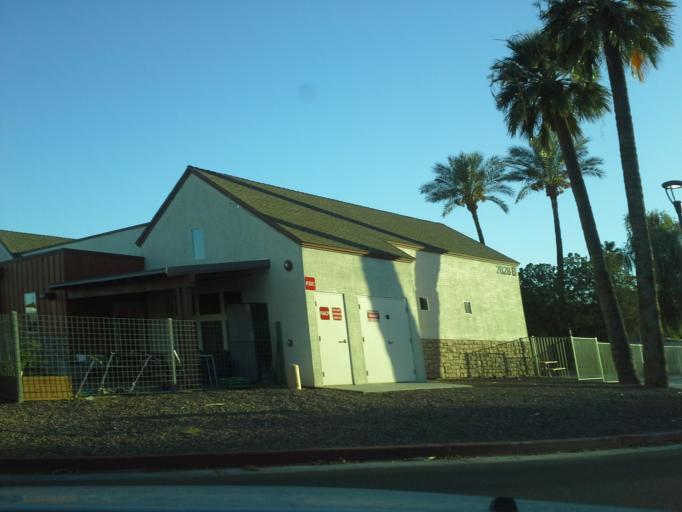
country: US
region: Arizona
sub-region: Maricopa County
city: Phoenix
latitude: 33.5050
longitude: -112.0196
